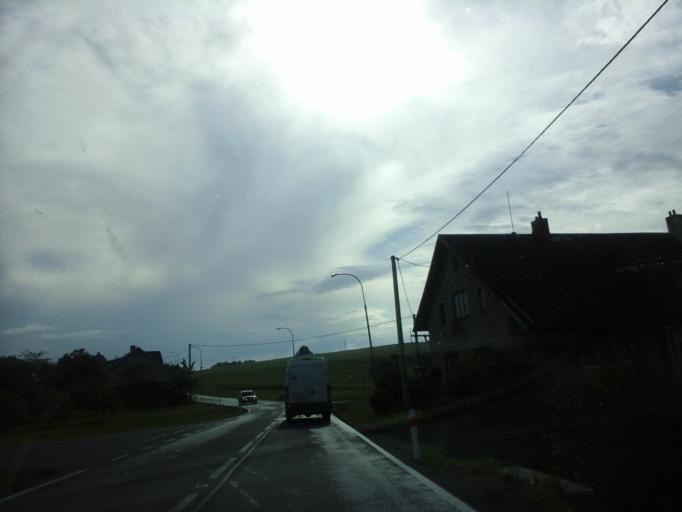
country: CZ
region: Olomoucky
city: Stity
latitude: 49.9528
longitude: 16.6935
